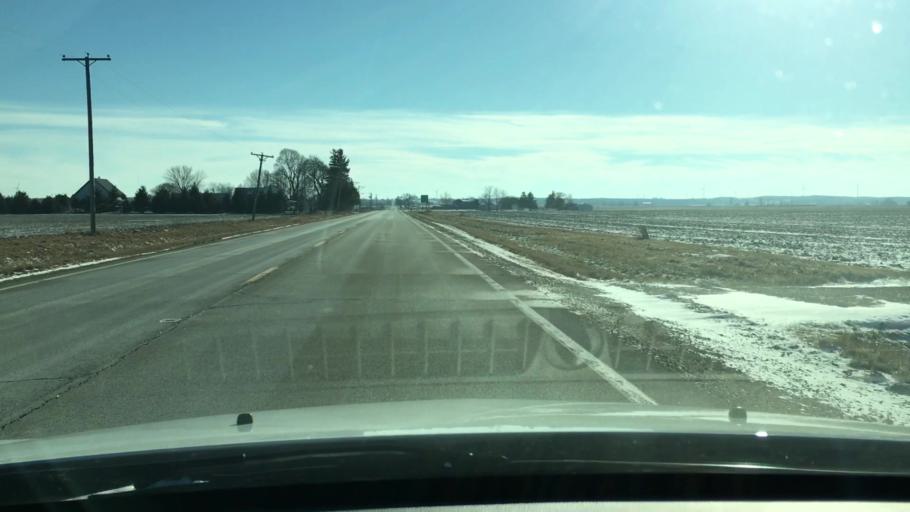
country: US
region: Illinois
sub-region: Ogle County
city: Rochelle
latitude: 41.7654
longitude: -89.0837
